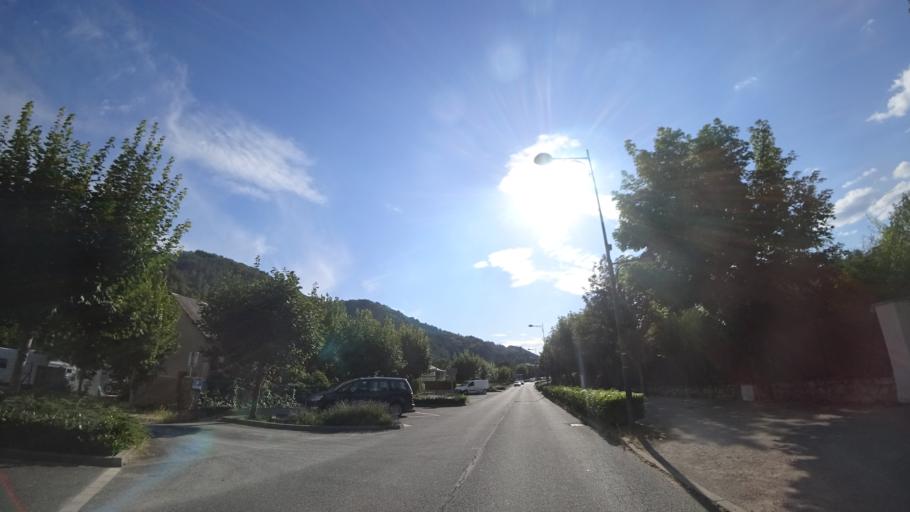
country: FR
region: Languedoc-Roussillon
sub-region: Departement de la Lozere
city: La Canourgue
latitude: 44.4335
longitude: 3.2119
